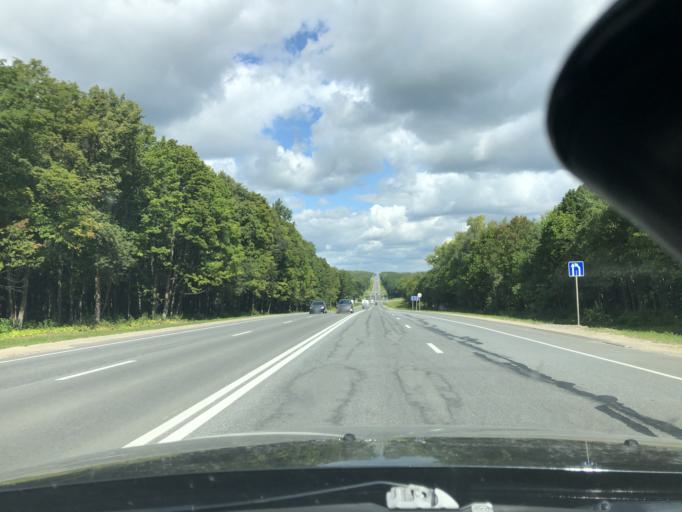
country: RU
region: Tula
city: Gorelki
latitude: 54.3157
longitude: 37.5636
